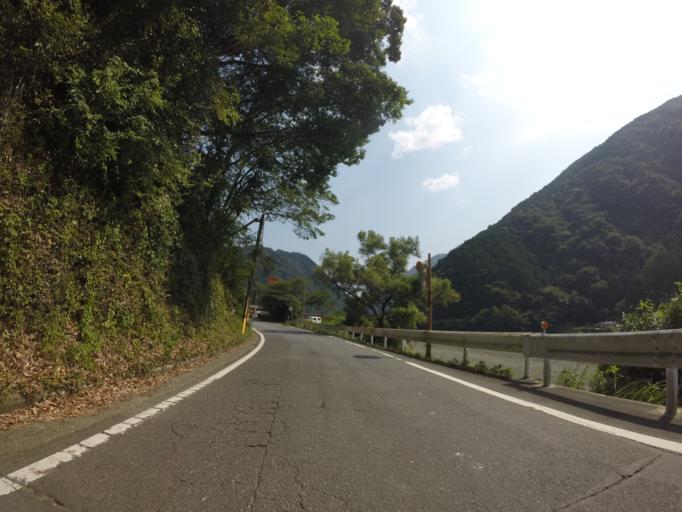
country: JP
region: Shizuoka
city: Shizuoka-shi
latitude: 35.1851
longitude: 138.3617
